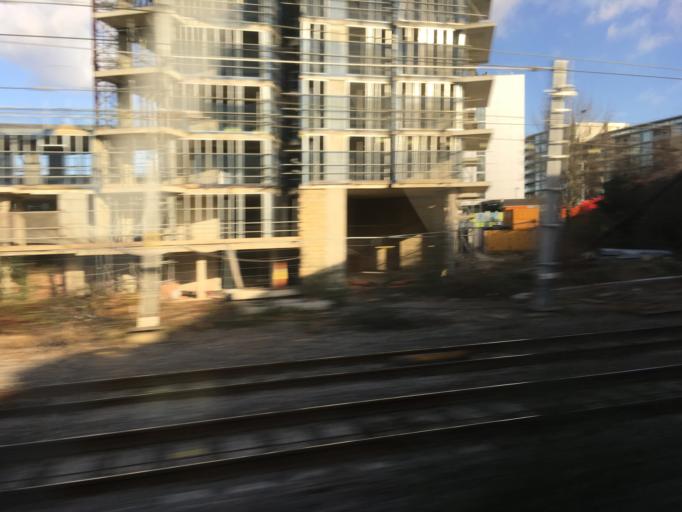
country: GB
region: England
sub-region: Greater London
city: Hayes
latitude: 51.5031
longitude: -0.4222
